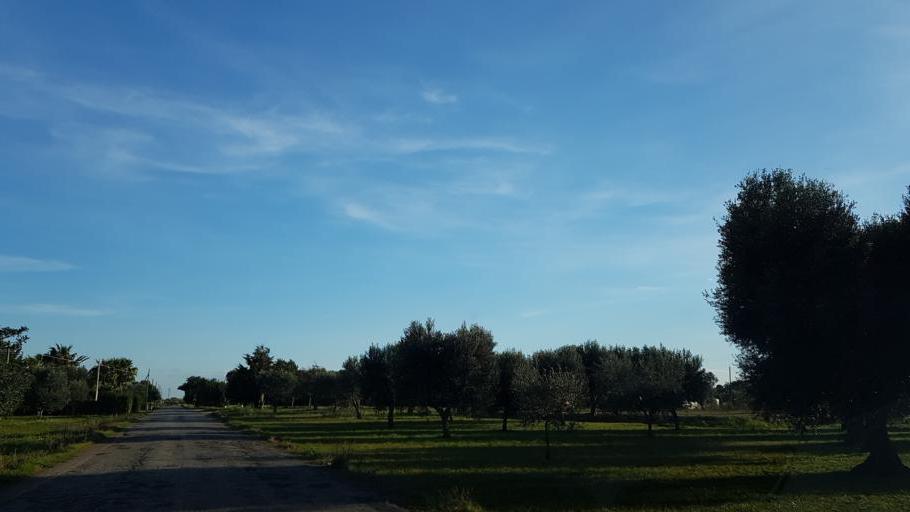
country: IT
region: Apulia
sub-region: Provincia di Brindisi
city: San Vito dei Normanni
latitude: 40.6716
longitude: 17.7772
